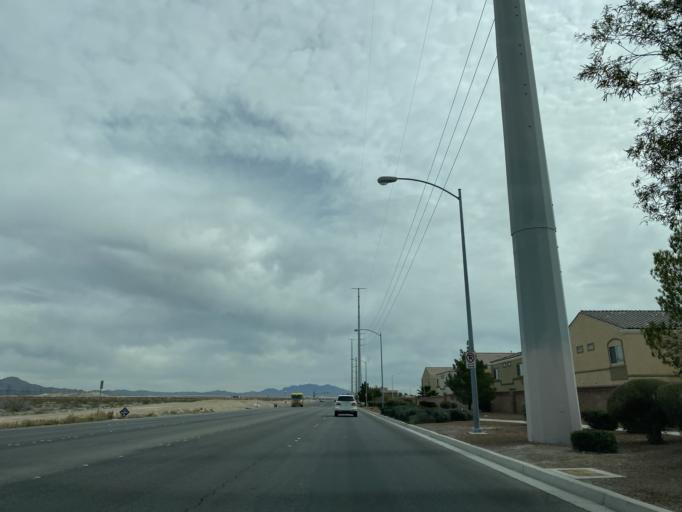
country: US
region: Nevada
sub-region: Clark County
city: Nellis Air Force Base
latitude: 36.2766
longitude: -115.0864
